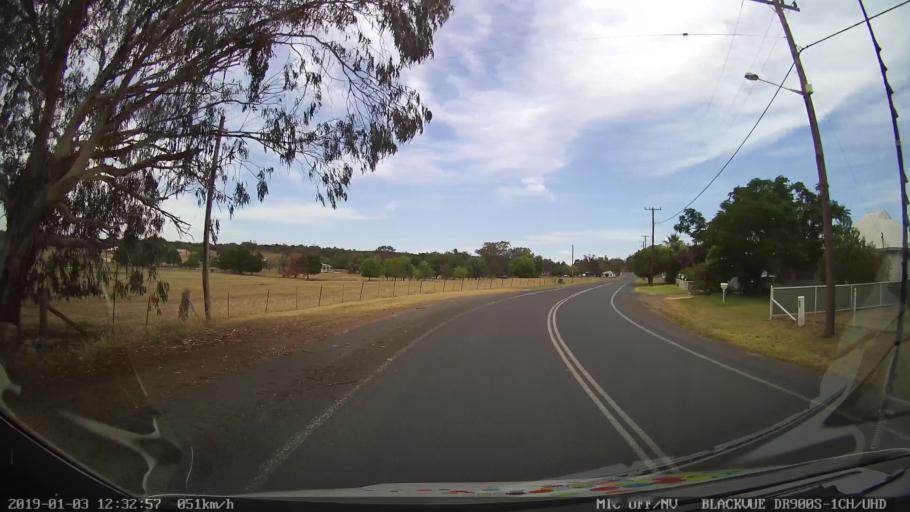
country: AU
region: New South Wales
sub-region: Weddin
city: Grenfell
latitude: -33.8890
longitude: 148.1622
